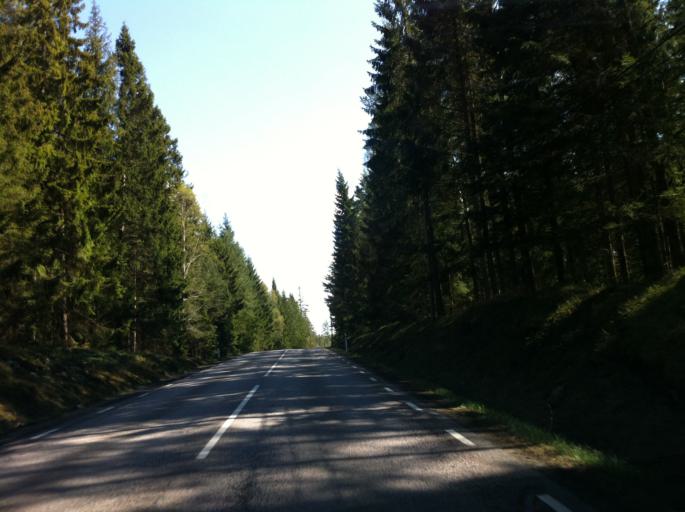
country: SE
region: Vaestra Goetaland
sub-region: Alingsas Kommun
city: Alingsas
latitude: 57.8512
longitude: 12.6348
